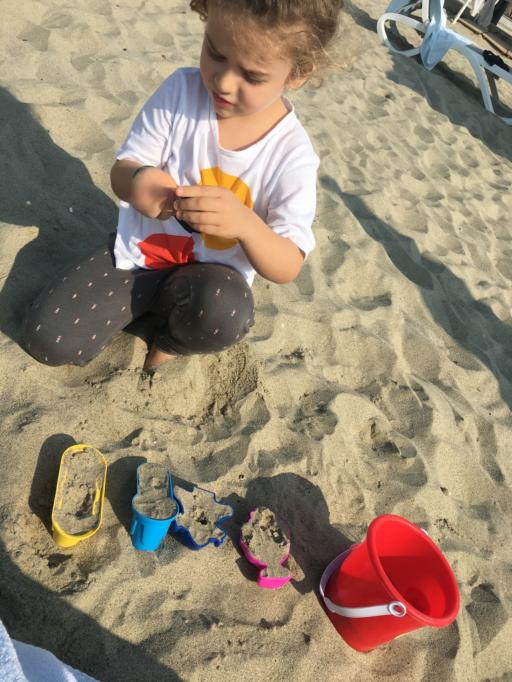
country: AL
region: Tirane
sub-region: Rrethi i Kavajes
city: Golem
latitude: 41.2625
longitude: 19.5195
